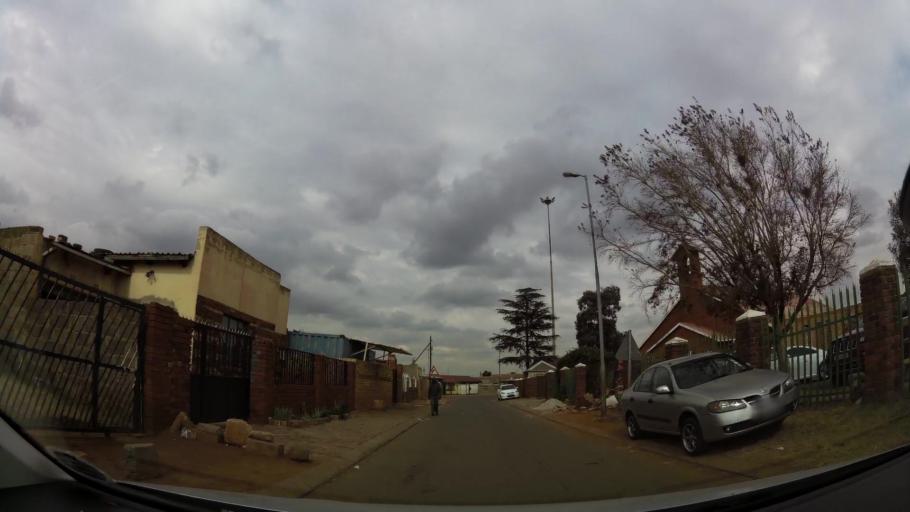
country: ZA
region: Gauteng
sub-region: City of Johannesburg Metropolitan Municipality
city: Soweto
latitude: -26.2752
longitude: 27.8580
